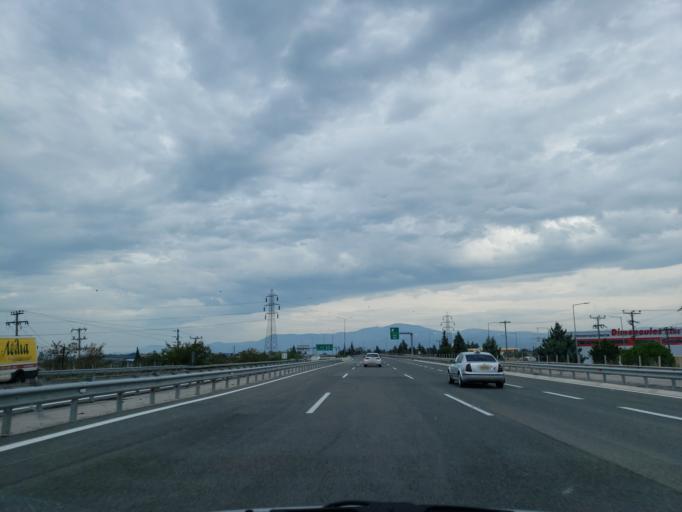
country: GR
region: Central Greece
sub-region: Nomos Voiotias
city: Schimatari
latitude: 38.3329
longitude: 23.6011
